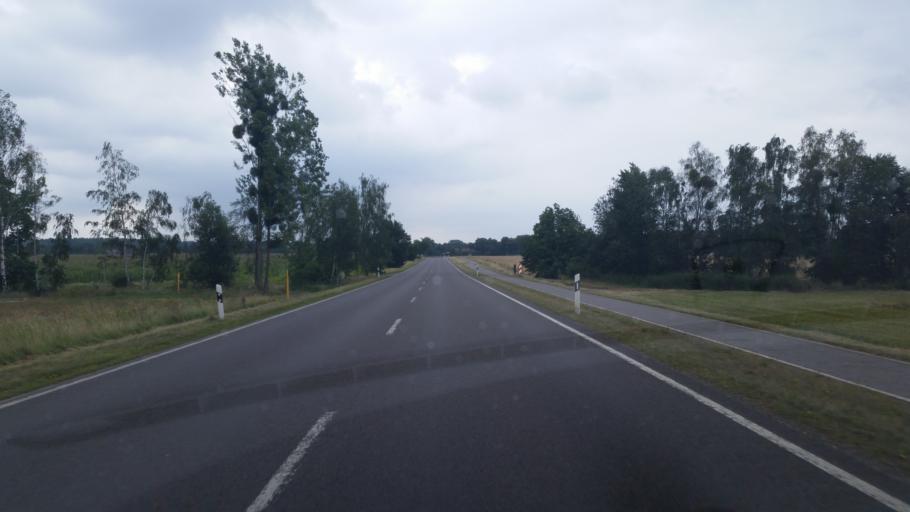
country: DE
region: Brandenburg
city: Hohenbocka
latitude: 51.4714
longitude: 14.0679
